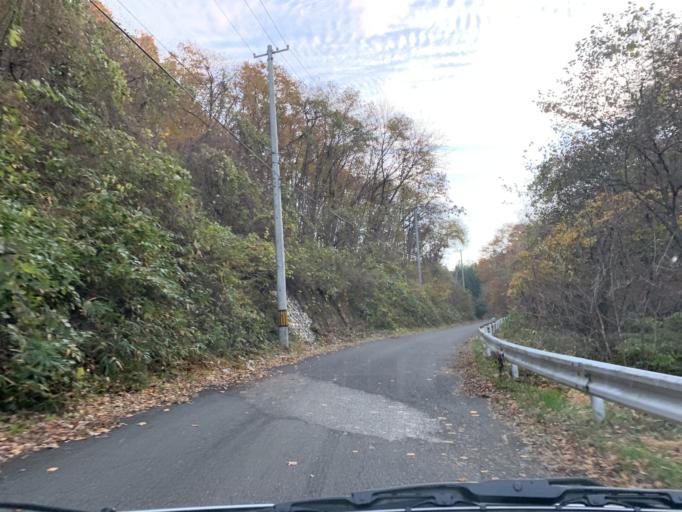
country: JP
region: Iwate
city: Ichinoseki
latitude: 39.0016
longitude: 141.0062
